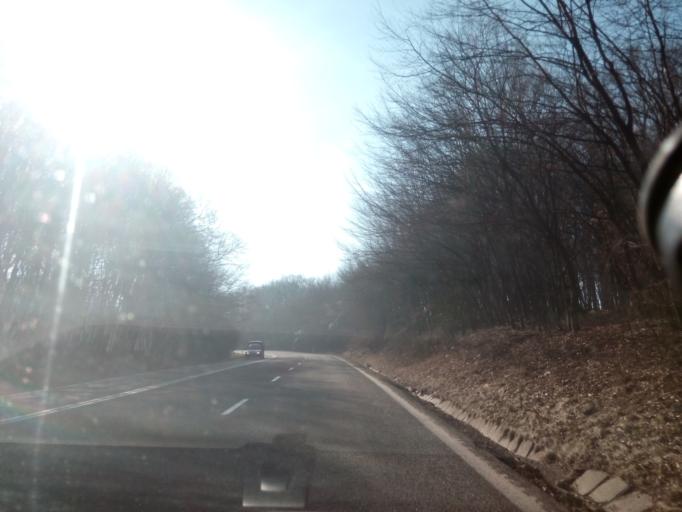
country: SK
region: Kosicky
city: Kosice
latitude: 48.7334
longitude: 21.3810
